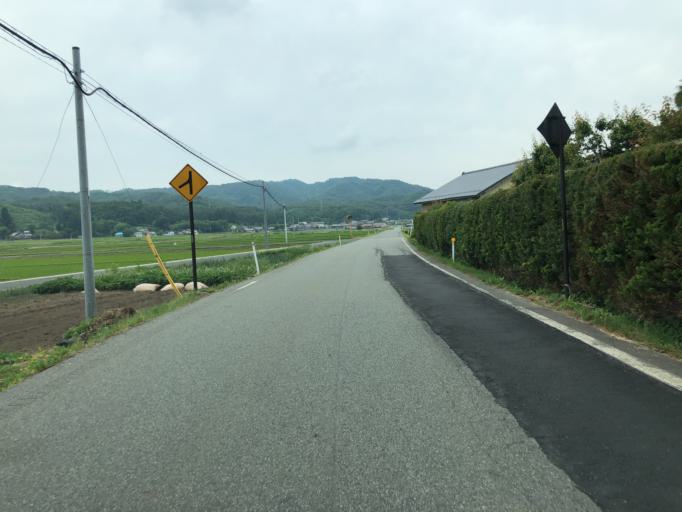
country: JP
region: Fukushima
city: Funehikimachi-funehiki
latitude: 37.3487
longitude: 140.7952
